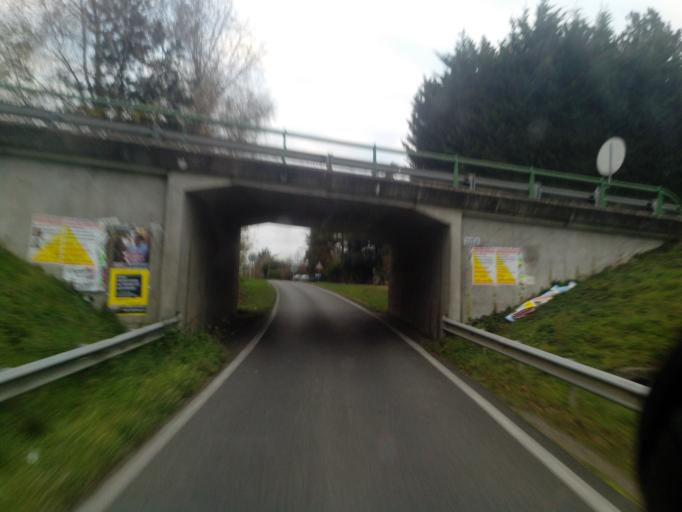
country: FR
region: Poitou-Charentes
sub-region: Departement de la Vienne
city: Mignaloux-Beauvoir
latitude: 46.5653
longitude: 0.3978
